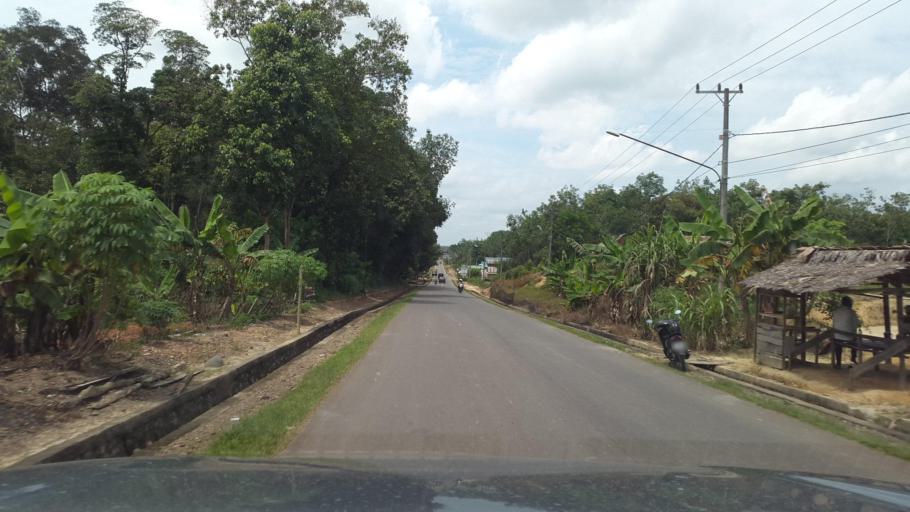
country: ID
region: South Sumatra
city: Gunungmegang Dalam
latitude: -3.3141
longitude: 103.8896
